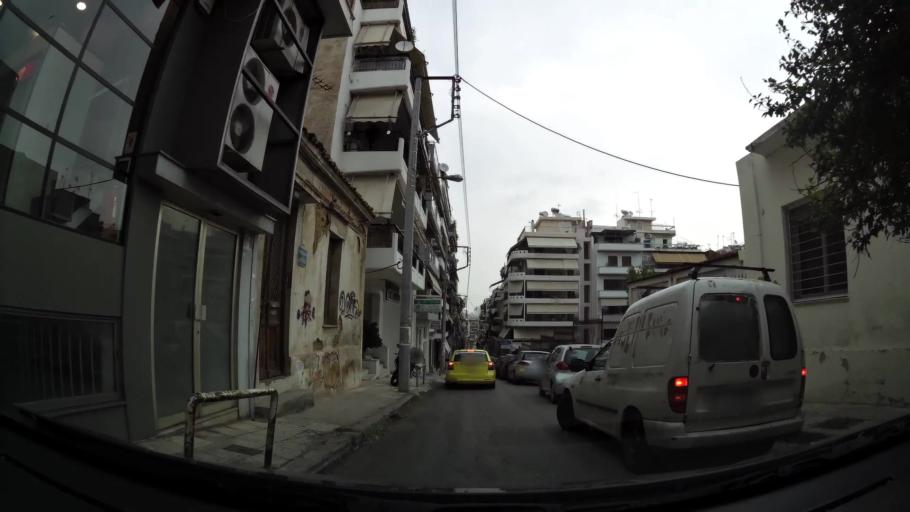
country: GR
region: Attica
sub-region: Nomos Attikis
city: Piraeus
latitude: 37.9299
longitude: 23.6435
